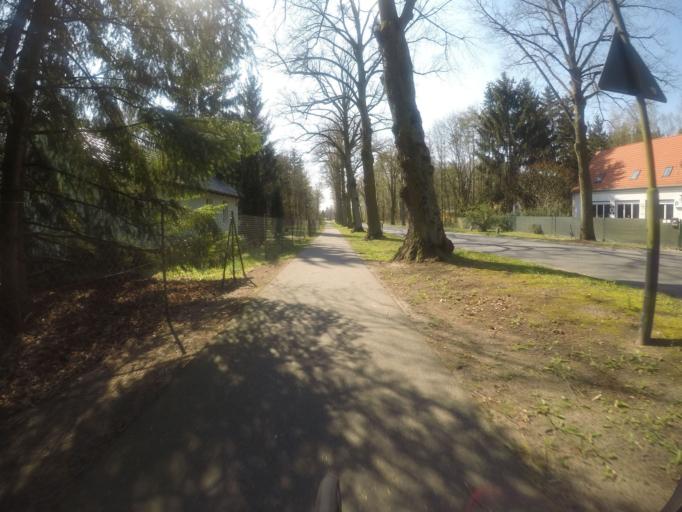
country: DE
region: Brandenburg
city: Brieselang
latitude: 52.6498
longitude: 13.0057
